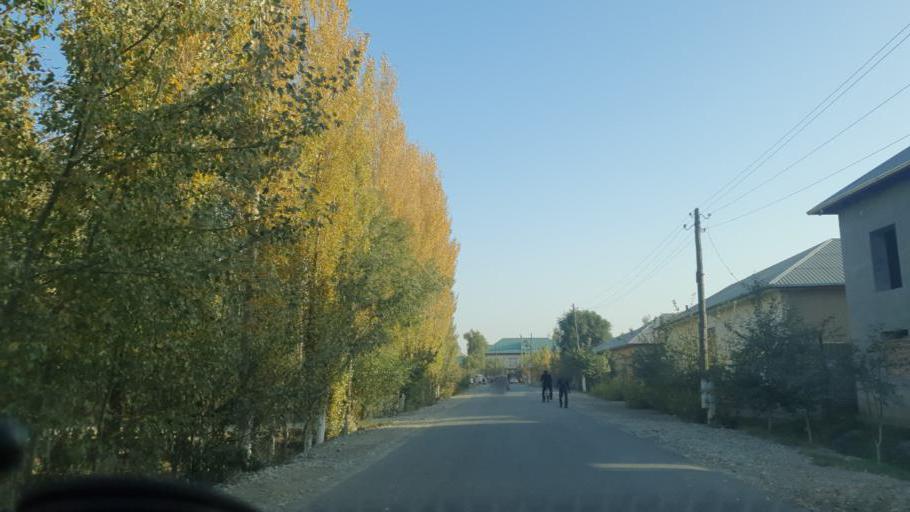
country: UZ
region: Fergana
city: Beshariq
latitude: 40.4632
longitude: 70.5434
